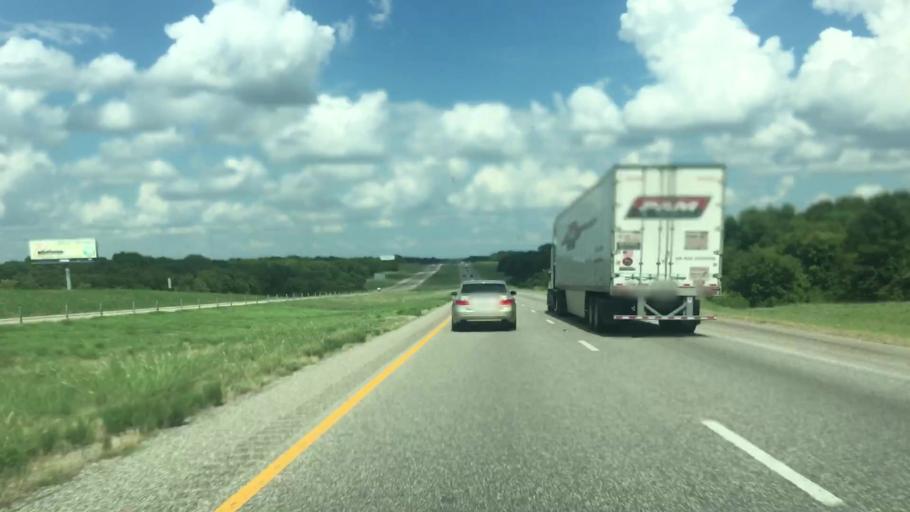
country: US
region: Texas
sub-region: Hill County
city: Hillsboro
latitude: 32.0855
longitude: -97.0402
